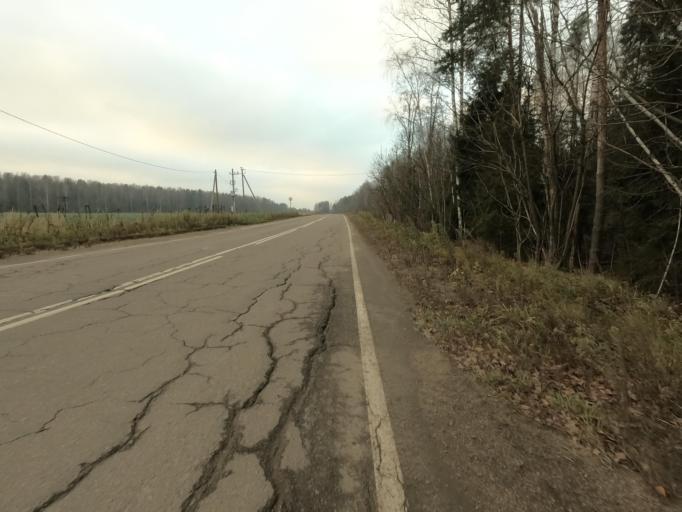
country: RU
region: Leningrad
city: Mga
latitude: 59.7981
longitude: 31.0013
